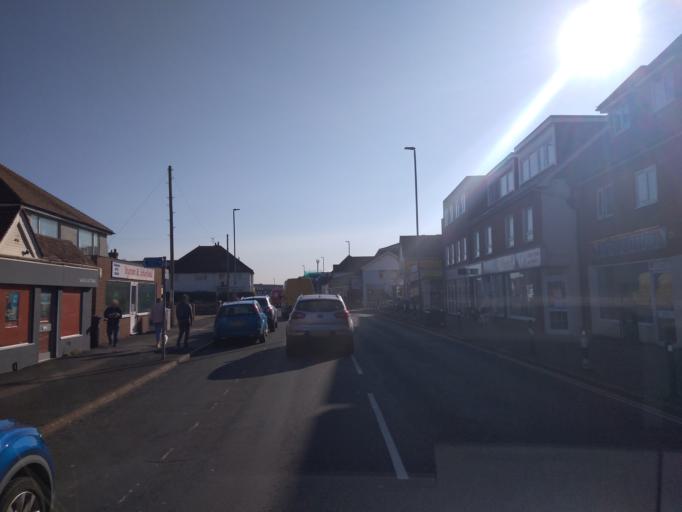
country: GB
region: England
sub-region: East Sussex
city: Peacehaven
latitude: 50.7914
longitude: -0.0018
